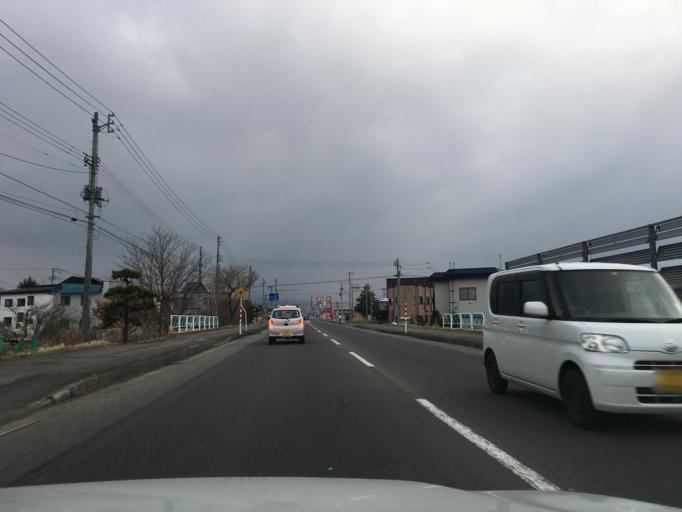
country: JP
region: Aomori
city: Kuroishi
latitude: 40.5884
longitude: 140.5690
